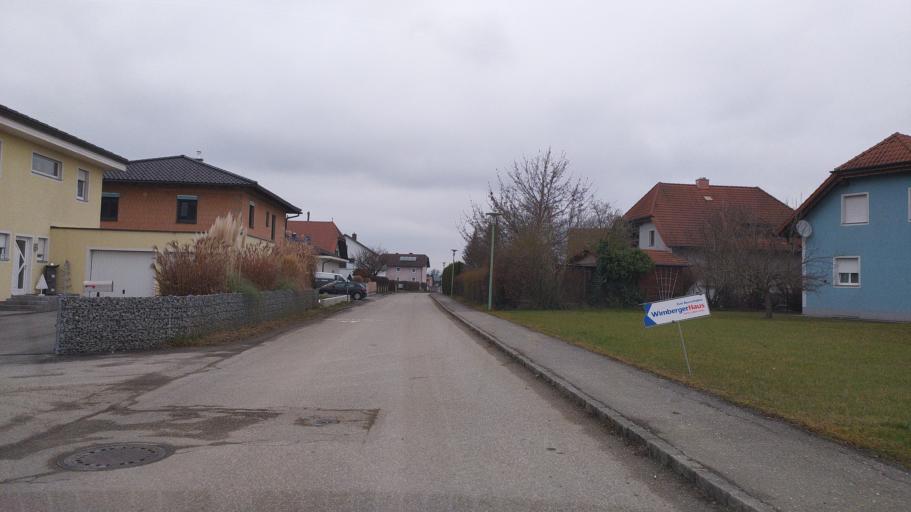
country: AT
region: Upper Austria
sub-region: Politischer Bezirk Urfahr-Umgebung
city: Feldkirchen an der Donau
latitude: 48.3068
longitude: 14.0063
